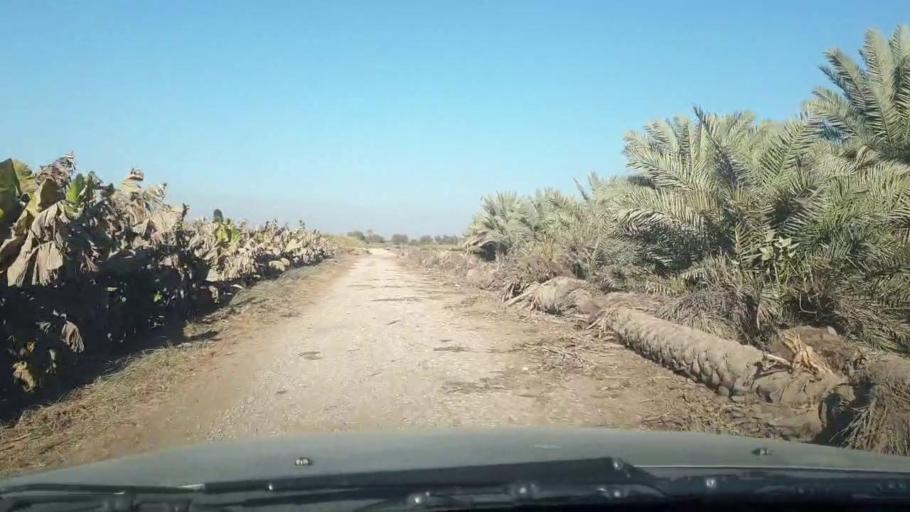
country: PK
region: Sindh
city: Adilpur
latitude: 27.9511
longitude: 69.1972
